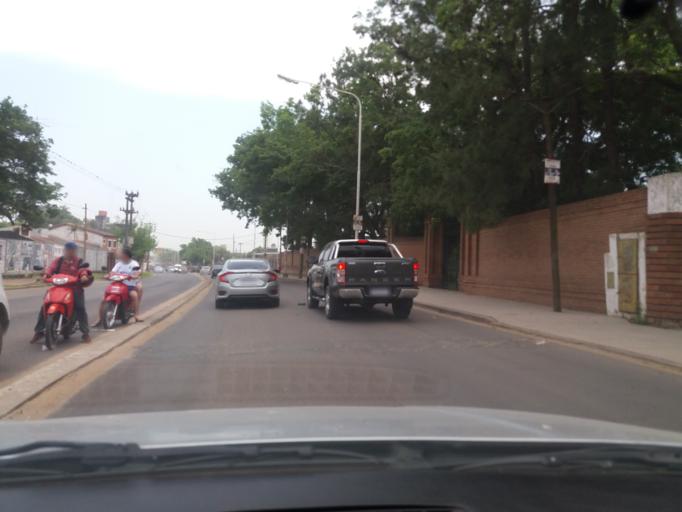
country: AR
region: Corrientes
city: Corrientes
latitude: -27.5015
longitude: -58.8130
